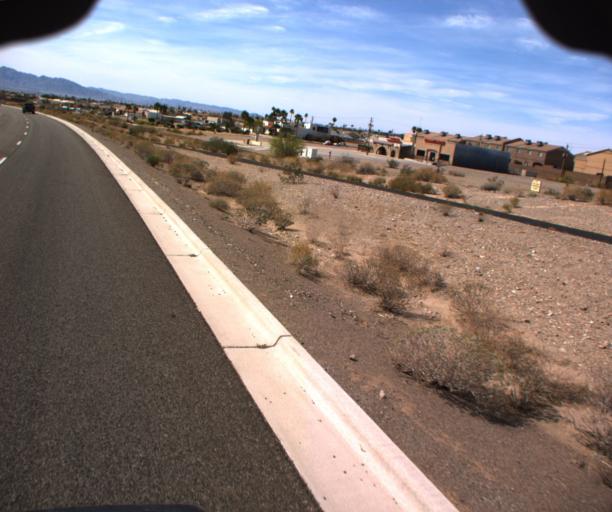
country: US
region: Arizona
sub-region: Mohave County
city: Lake Havasu City
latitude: 34.4560
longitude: -114.2699
